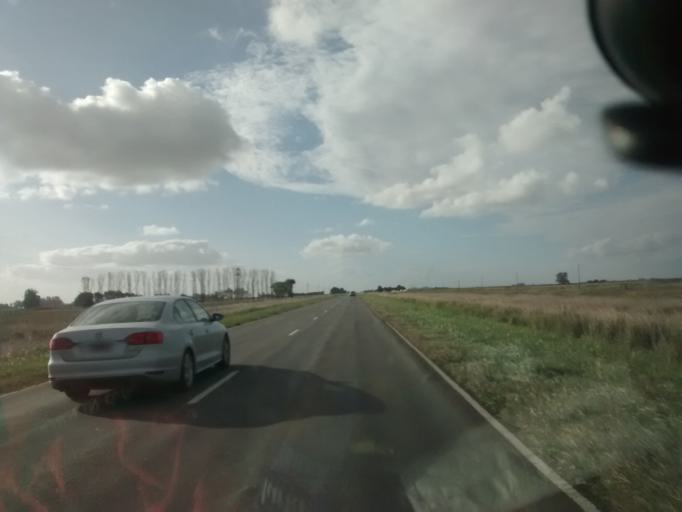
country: AR
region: Buenos Aires
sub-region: Partido de Ayacucho
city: Ayacucho
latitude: -36.9004
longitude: -58.5303
